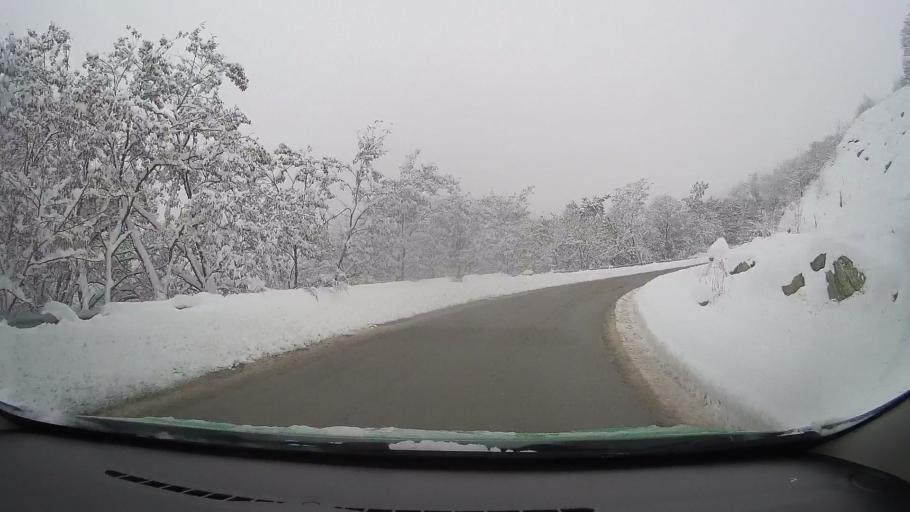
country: RO
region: Sibiu
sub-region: Comuna Jina
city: Jina
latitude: 45.7713
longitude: 23.6655
